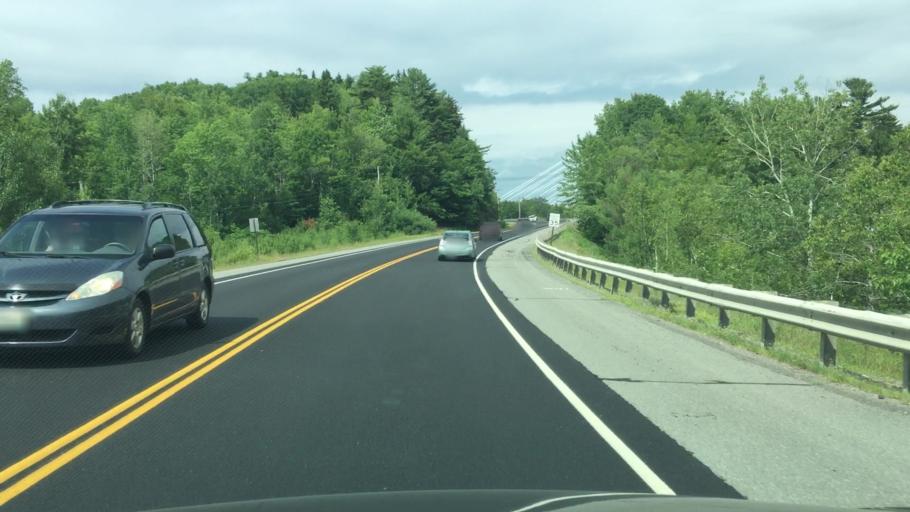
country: US
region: Maine
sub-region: Hancock County
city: Bucksport
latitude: 44.5553
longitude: -68.8097
